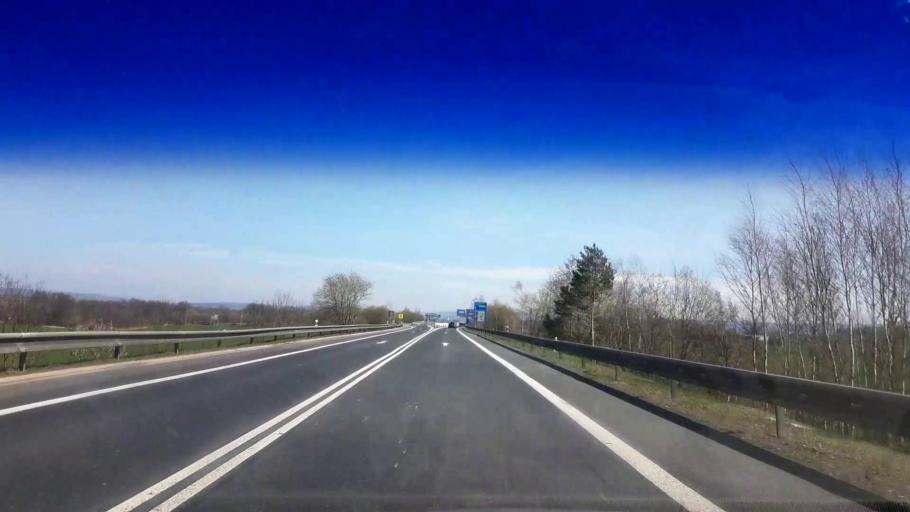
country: CZ
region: Karlovarsky
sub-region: Okres Cheb
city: Cheb
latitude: 50.0957
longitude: 12.3578
